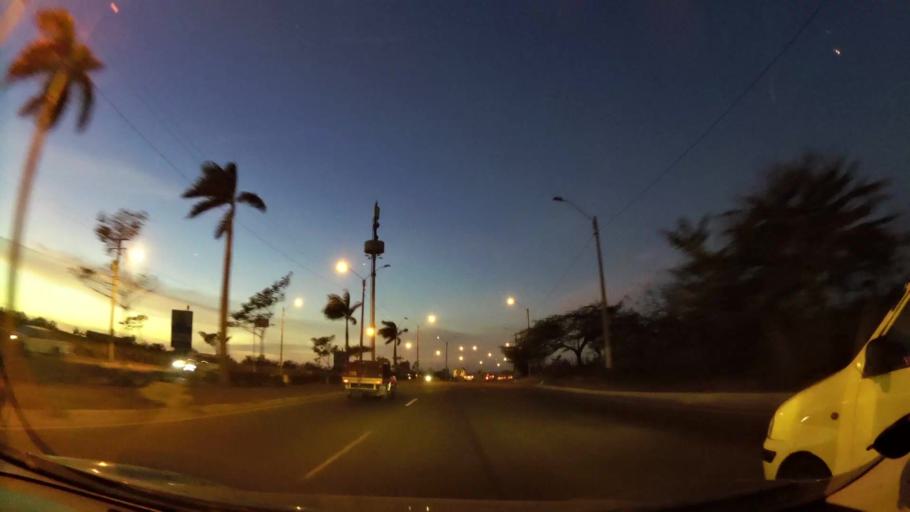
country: CO
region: Atlantico
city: Barranquilla
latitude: 10.9306
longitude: -74.8322
